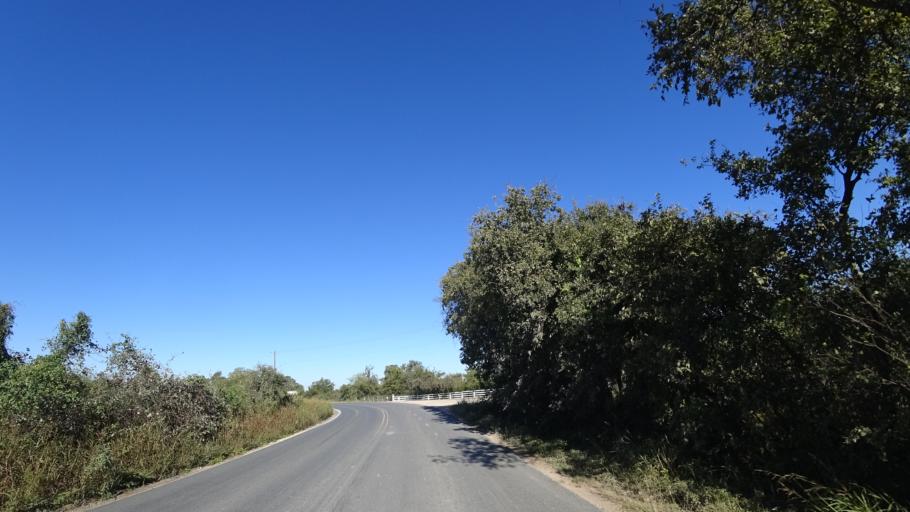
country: US
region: Texas
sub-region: Travis County
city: Austin
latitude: 30.2459
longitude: -97.6723
